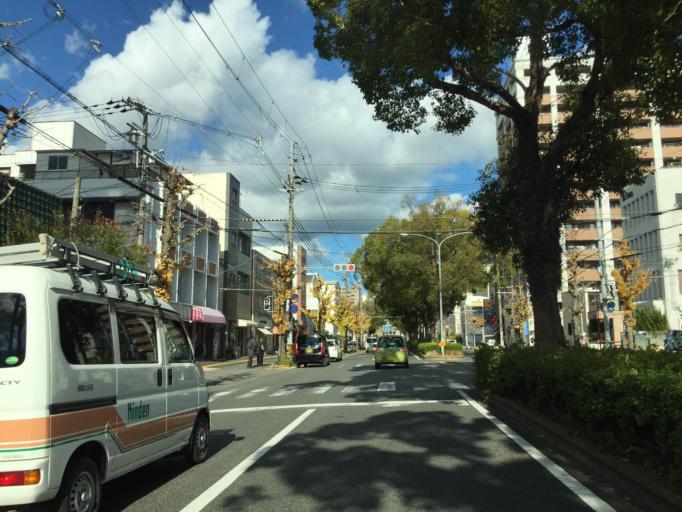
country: JP
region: Wakayama
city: Wakayama-shi
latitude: 34.2272
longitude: 135.1782
